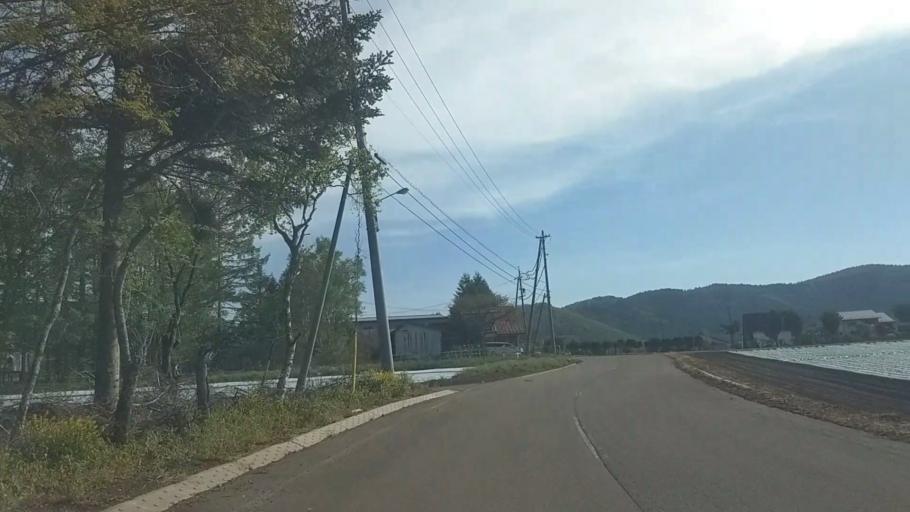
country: JP
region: Yamanashi
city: Nirasaki
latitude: 35.9416
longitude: 138.4780
